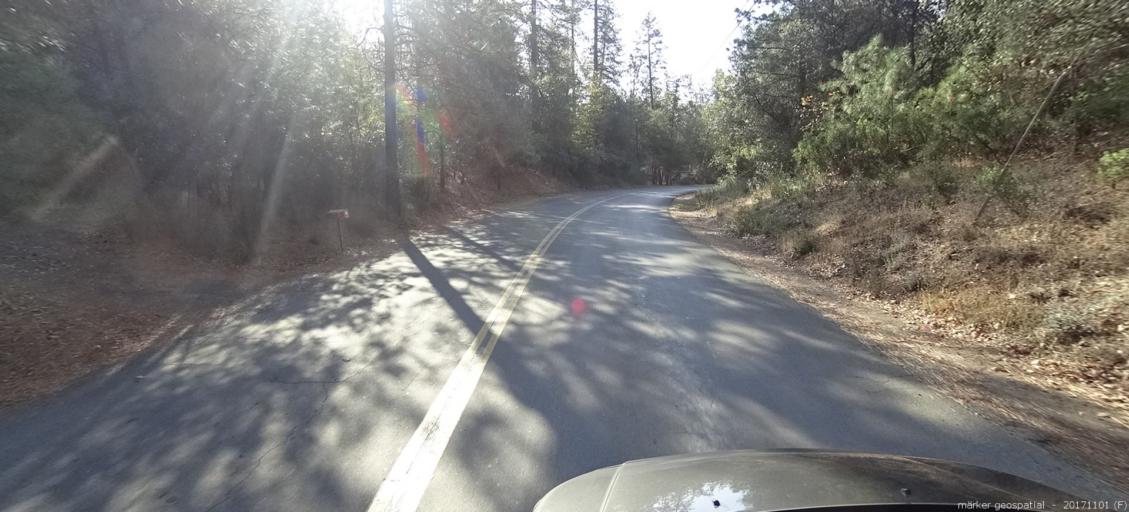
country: US
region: California
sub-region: Shasta County
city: Shasta Lake
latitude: 40.7318
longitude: -122.3182
